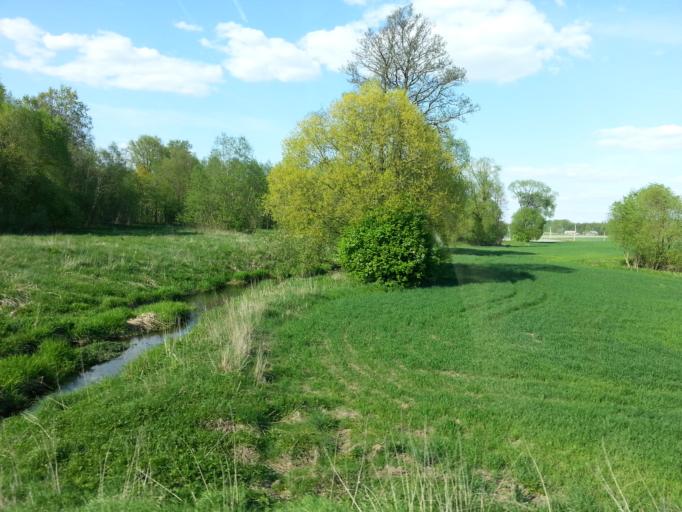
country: LT
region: Panevezys
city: Pasvalys
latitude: 56.0326
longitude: 24.3582
